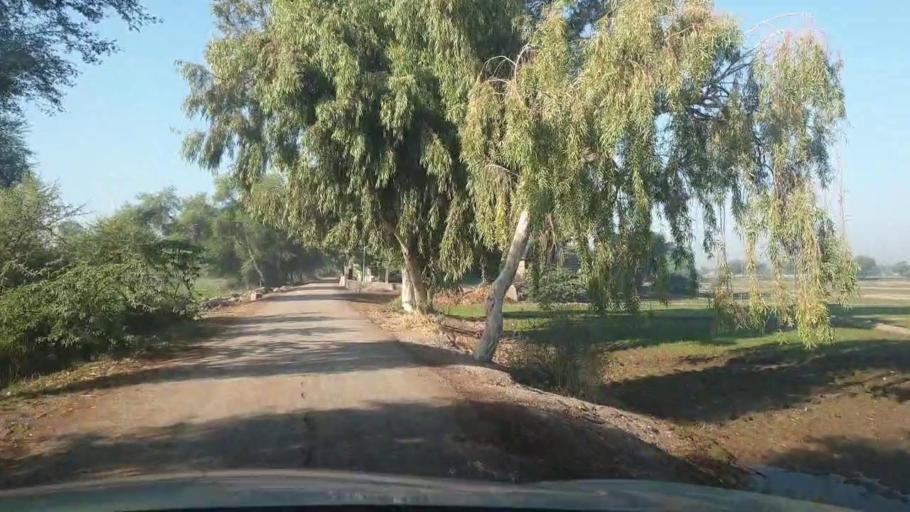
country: PK
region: Sindh
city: Bhan
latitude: 26.5524
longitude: 67.6857
